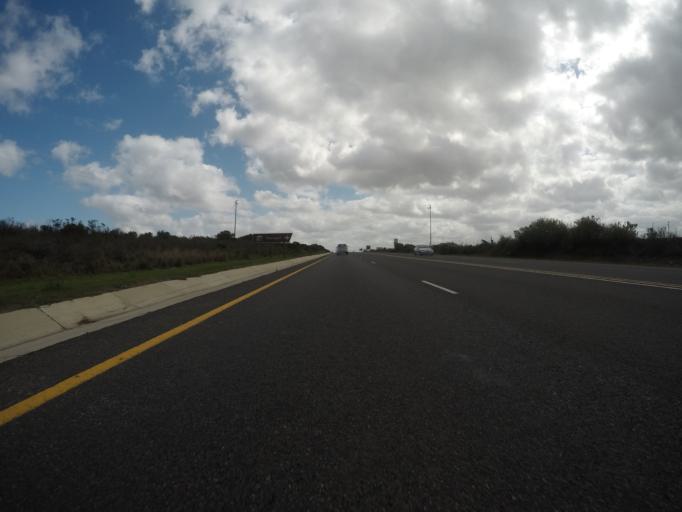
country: ZA
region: Western Cape
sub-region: Eden District Municipality
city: Mossel Bay
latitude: -34.1811
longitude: 22.0321
